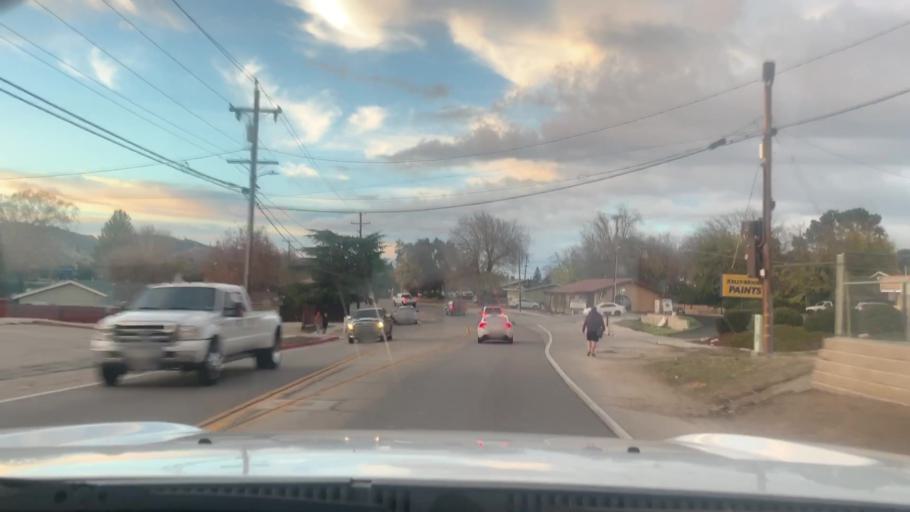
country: US
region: California
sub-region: San Luis Obispo County
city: Paso Robles
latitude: 35.6282
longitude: -120.6750
